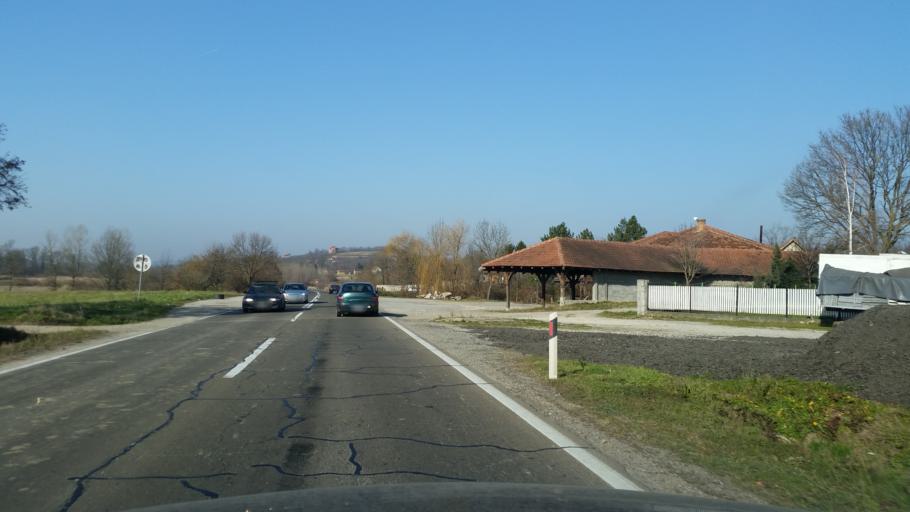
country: RS
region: Central Serbia
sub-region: Kolubarski Okrug
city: Ljig
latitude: 44.2763
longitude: 20.2814
